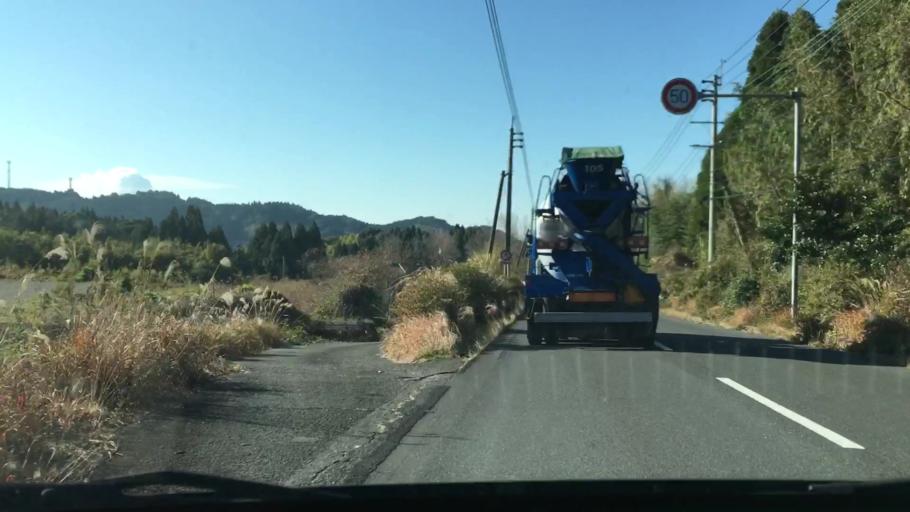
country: JP
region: Kagoshima
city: Kajiki
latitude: 31.7676
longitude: 130.6914
